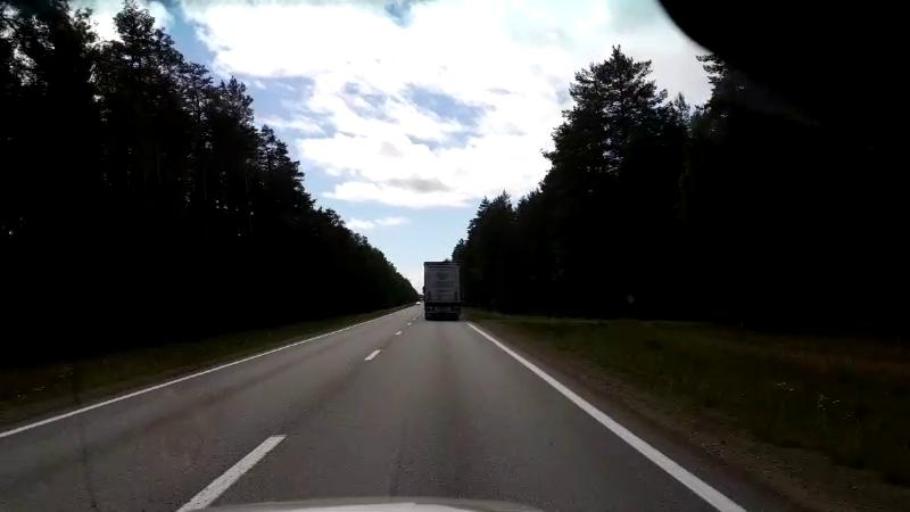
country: LV
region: Salacgrivas
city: Salacgriva
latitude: 57.5264
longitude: 24.4308
